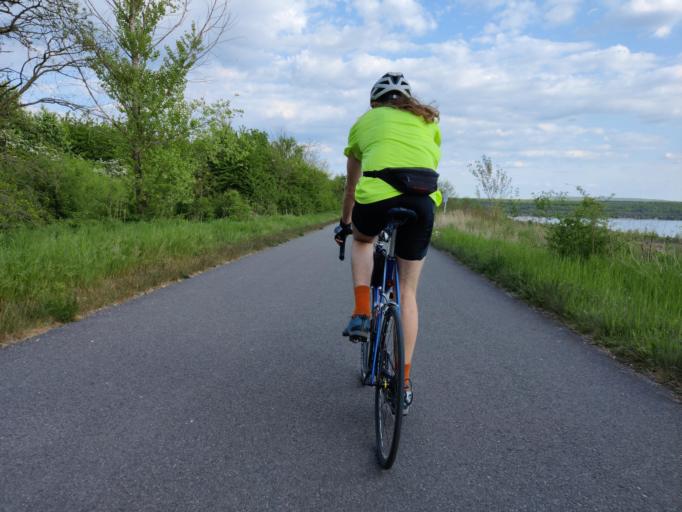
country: DE
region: Saxony
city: Grossposna
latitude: 51.2460
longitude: 12.4681
